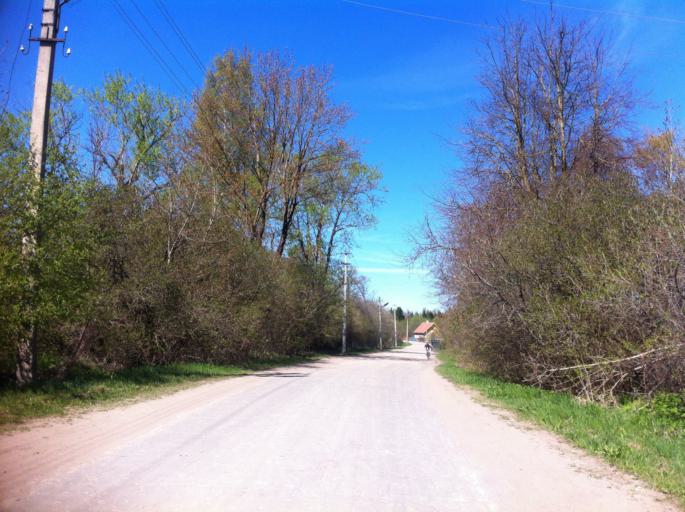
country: RU
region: Pskov
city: Izborsk
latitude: 57.7763
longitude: 27.9670
